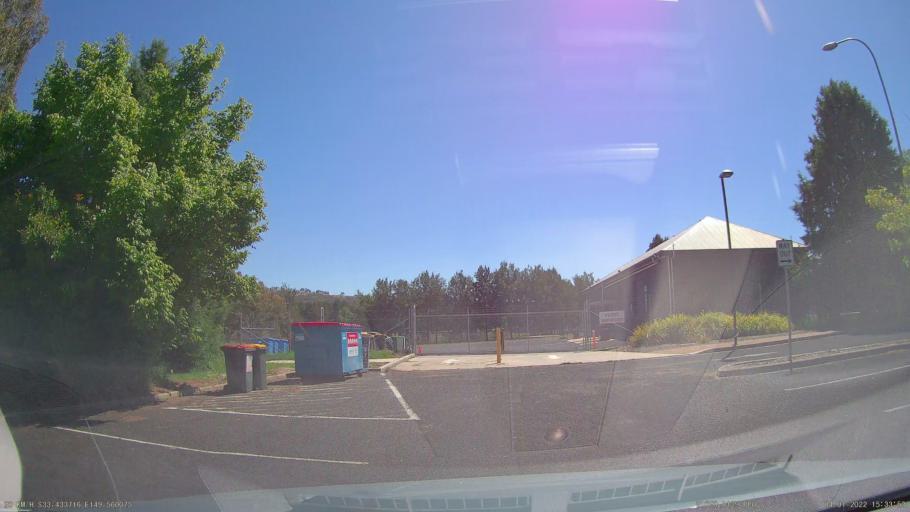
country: AU
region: New South Wales
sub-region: Bathurst Regional
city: Bathurst
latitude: -33.4338
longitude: 149.5600
